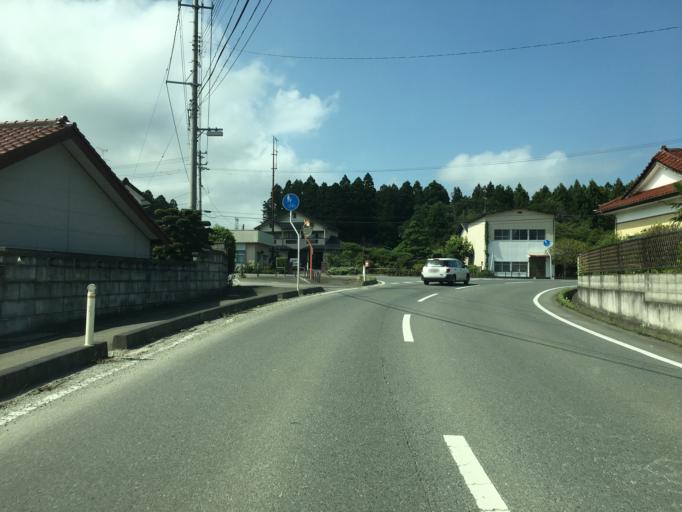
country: JP
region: Miyagi
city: Marumori
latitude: 37.8444
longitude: 140.8918
